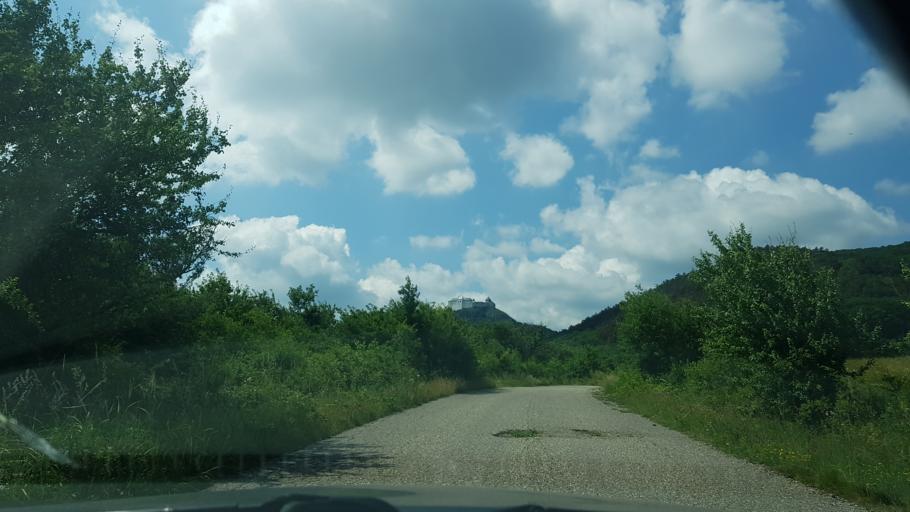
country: HU
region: Borsod-Abauj-Zemplen
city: Gonc
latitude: 48.5348
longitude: 21.4734
